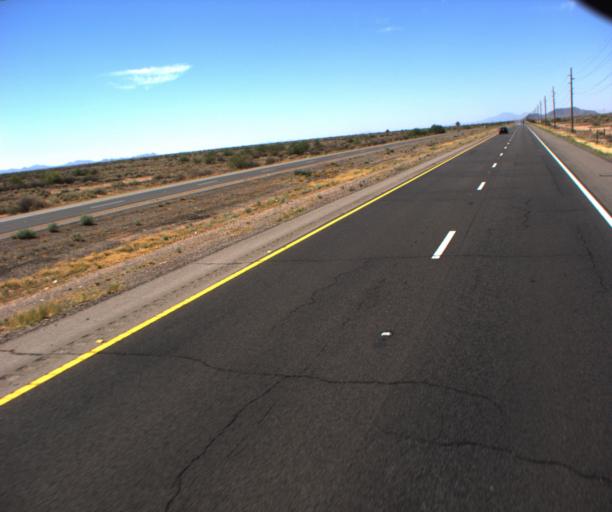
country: US
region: Arizona
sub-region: Maricopa County
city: Sun Lakes
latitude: 33.2452
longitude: -111.9804
